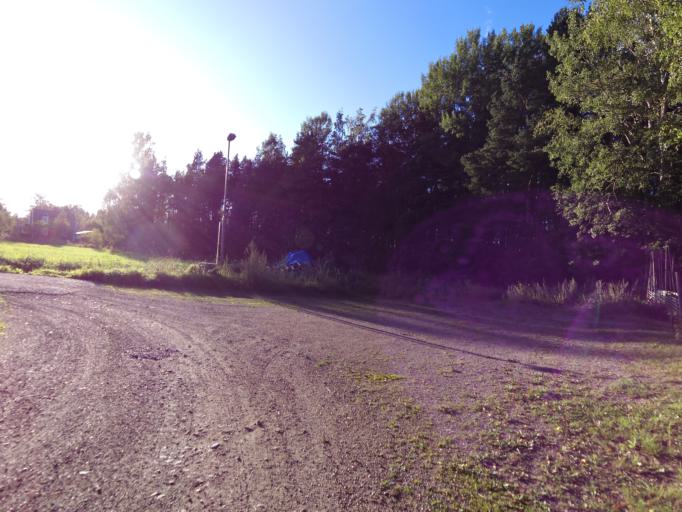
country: SE
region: Gaevleborg
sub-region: Gavle Kommun
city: Gavle
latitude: 60.7122
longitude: 17.1523
